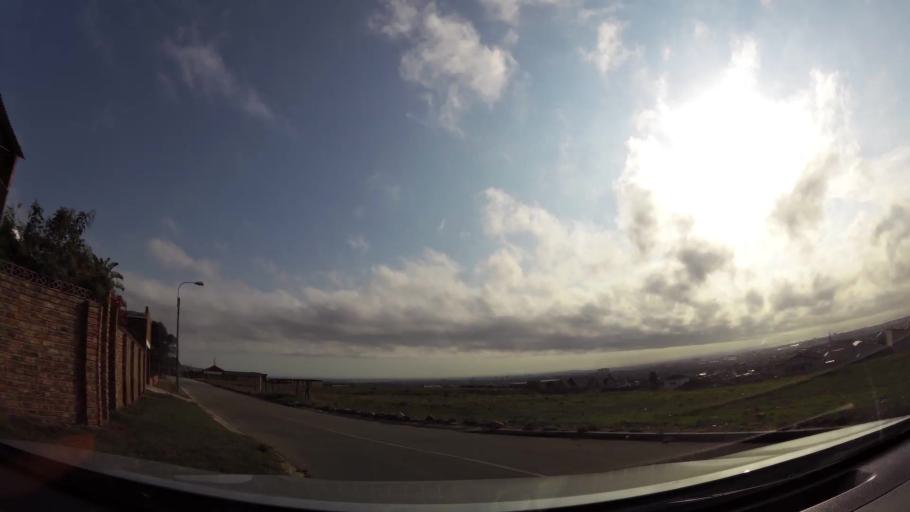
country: ZA
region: Eastern Cape
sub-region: Nelson Mandela Bay Metropolitan Municipality
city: Port Elizabeth
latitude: -33.9269
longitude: 25.5578
